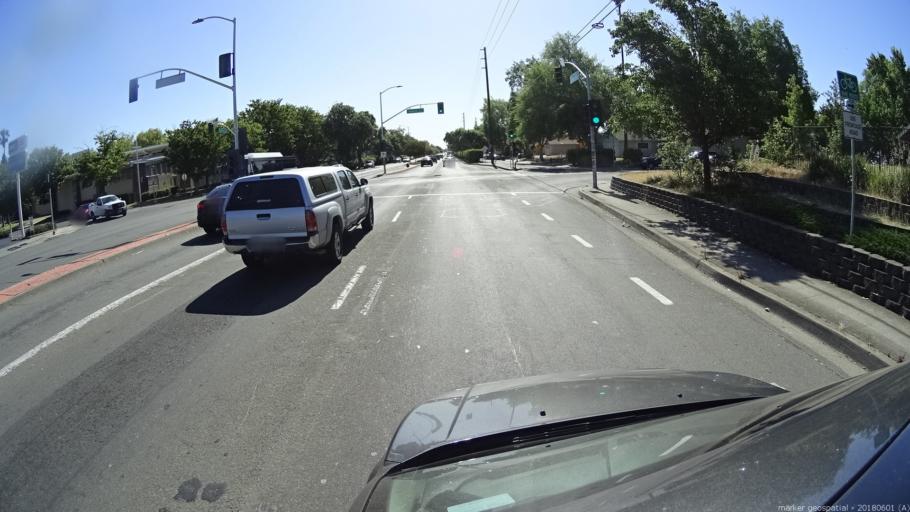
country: US
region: California
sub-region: Sacramento County
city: Parkway
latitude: 38.4956
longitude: -121.5038
